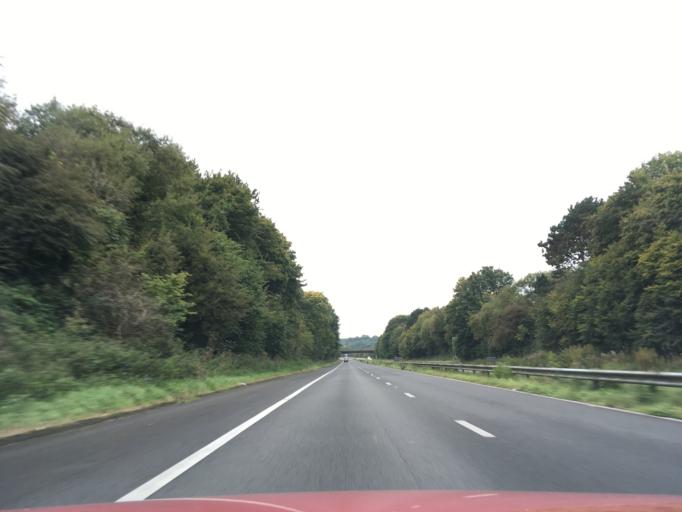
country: GB
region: Wales
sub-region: Monmouthshire
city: Chepstow
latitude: 51.6166
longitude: -2.7024
